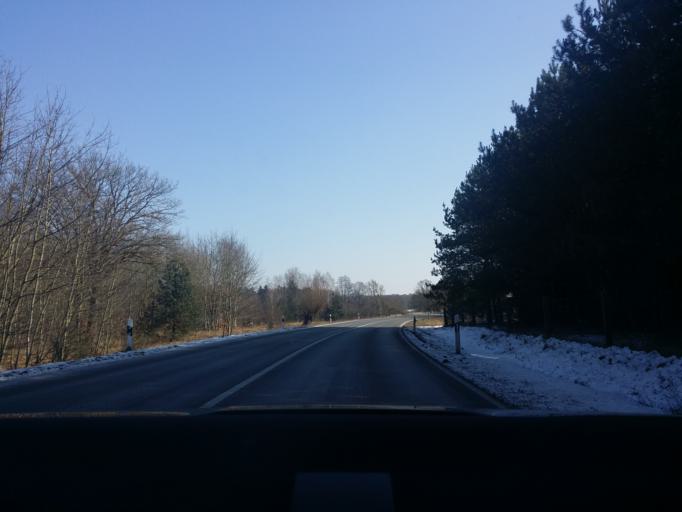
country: DE
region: Brandenburg
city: Gross Pankow
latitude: 53.1061
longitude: 11.9517
